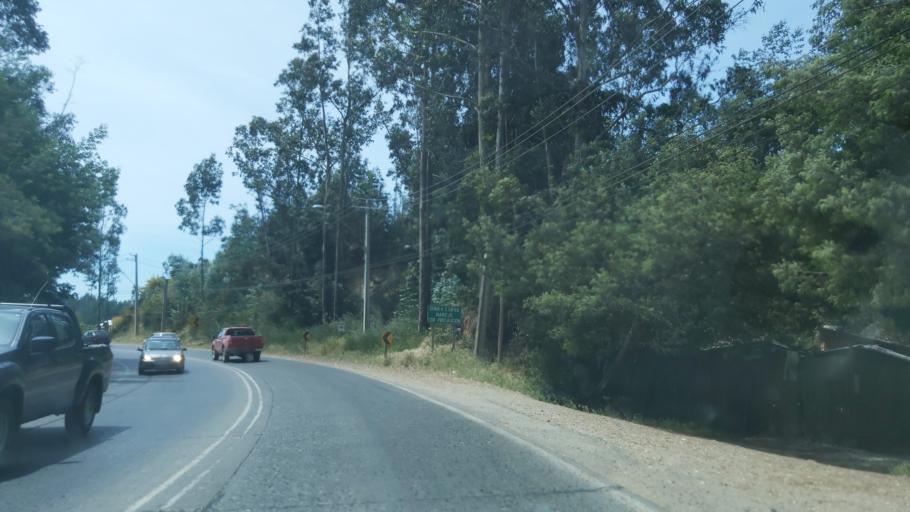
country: CL
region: Maule
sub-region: Provincia de Talca
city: Constitucion
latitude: -35.3511
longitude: -72.4085
